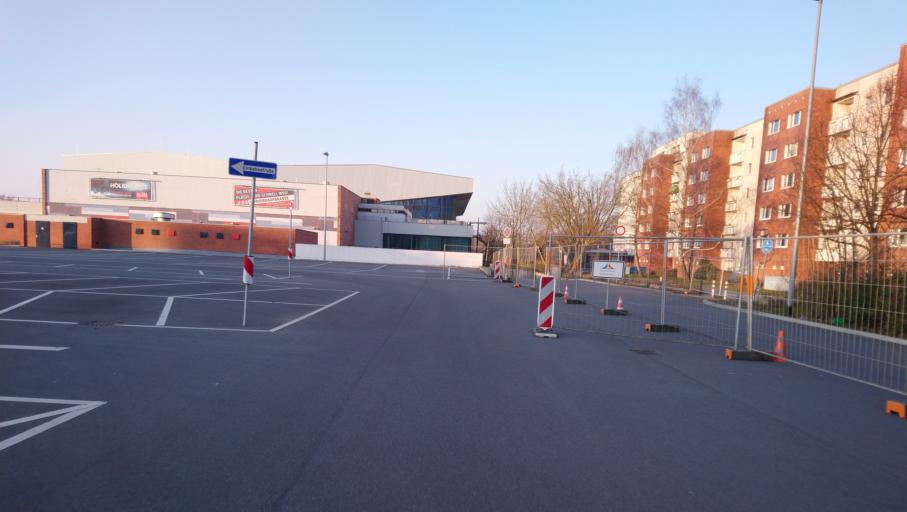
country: DE
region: Mecklenburg-Vorpommern
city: Rostock
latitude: 54.0758
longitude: 12.1249
